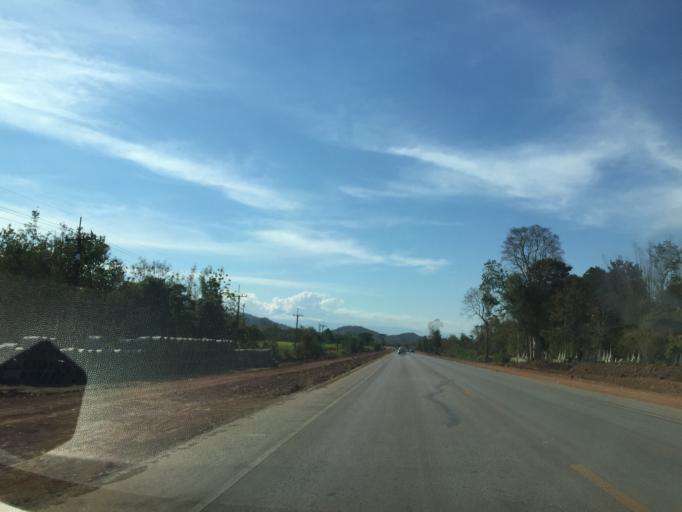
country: TH
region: Loei
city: Erawan
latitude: 17.2986
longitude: 101.8673
